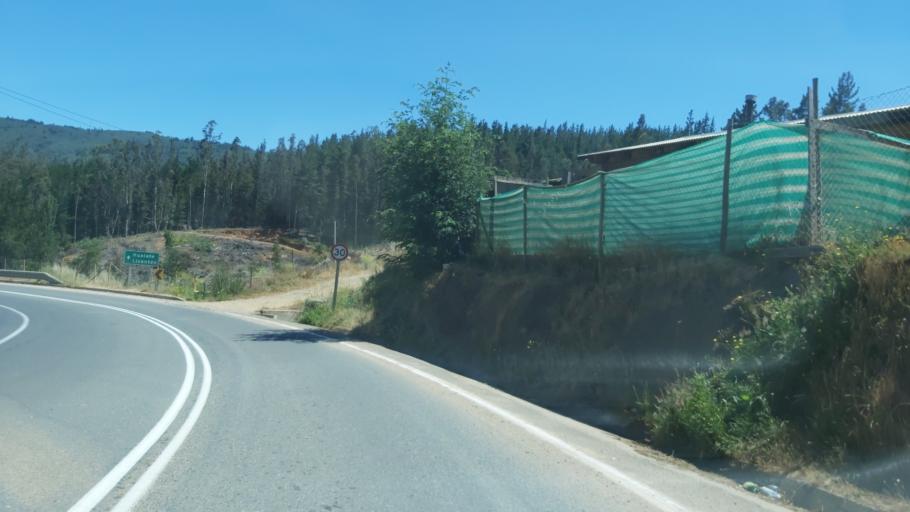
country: CL
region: Maule
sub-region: Provincia de Talca
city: Talca
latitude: -34.9846
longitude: -71.9743
